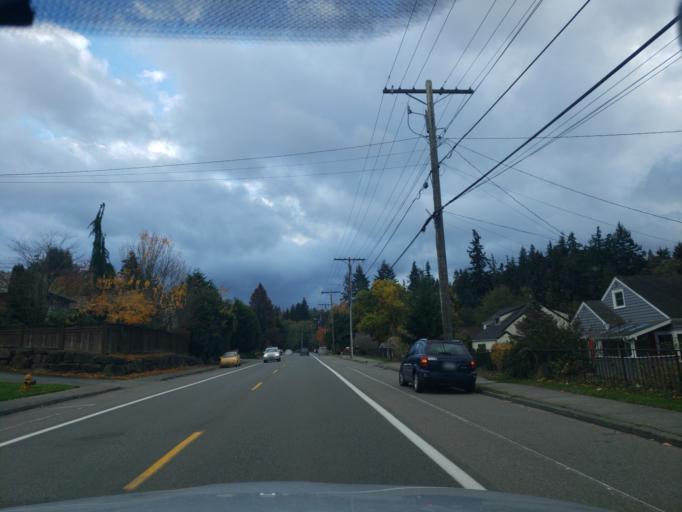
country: US
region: Washington
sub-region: Snohomish County
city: Everett
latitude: 47.9553
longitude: -122.2475
